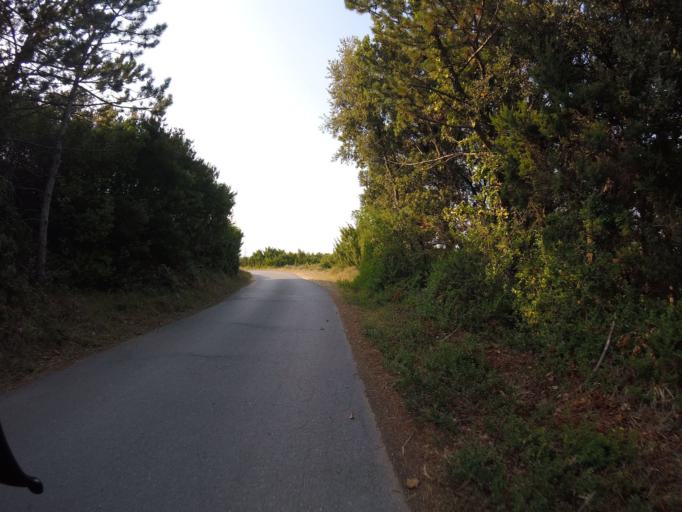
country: HR
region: Primorsko-Goranska
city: Lopar
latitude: 44.8401
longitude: 14.7312
